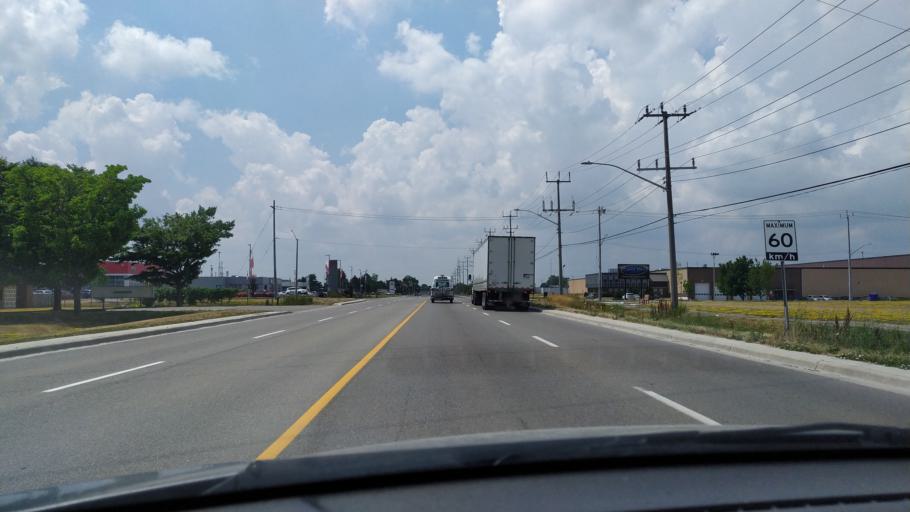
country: CA
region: Ontario
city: Stratford
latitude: 43.3521
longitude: -80.9992
